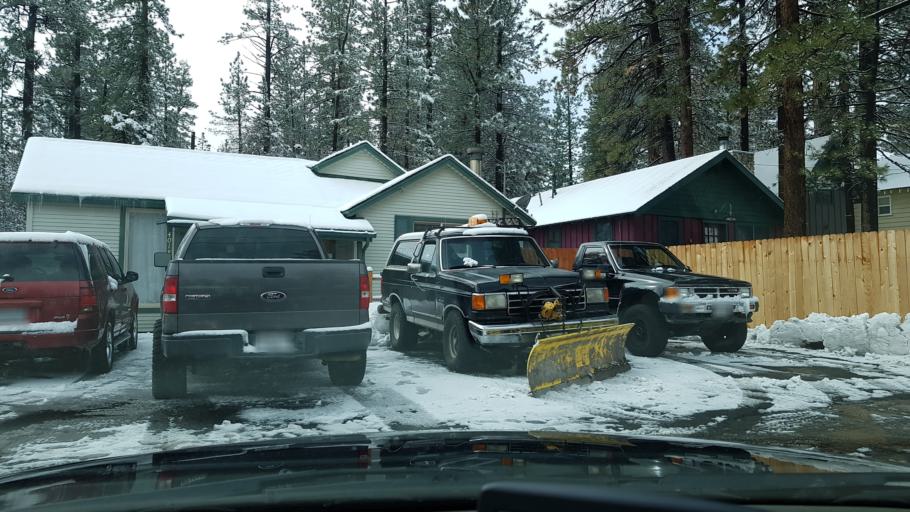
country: US
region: California
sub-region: San Bernardino County
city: Big Bear Lake
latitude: 34.2396
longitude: -116.9255
